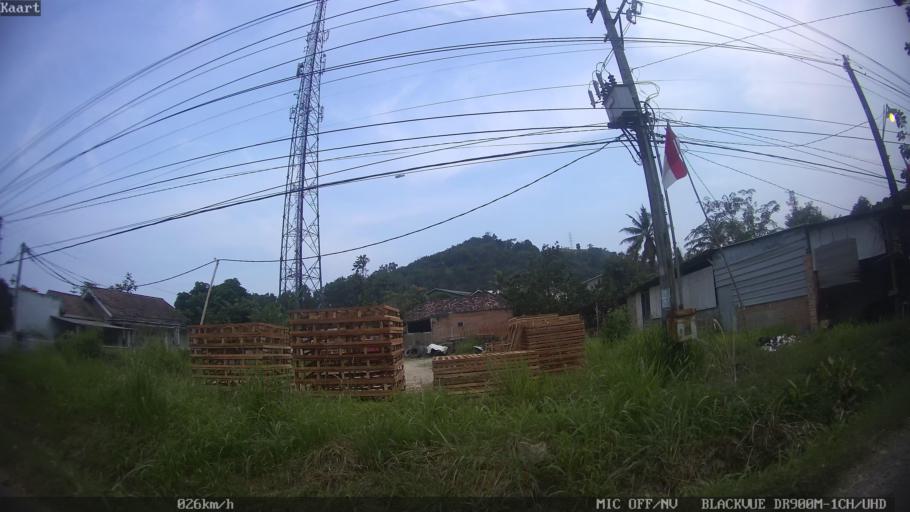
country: ID
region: Lampung
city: Panjang
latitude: -5.4184
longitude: 105.3309
